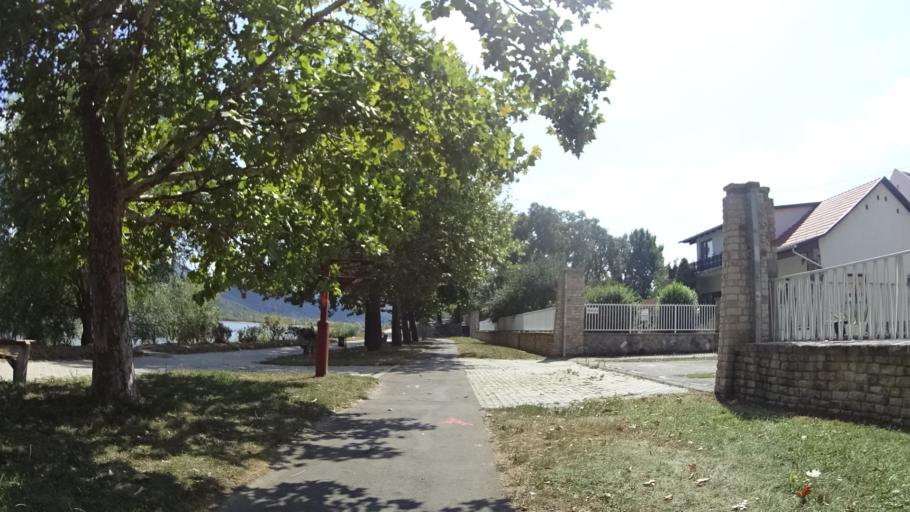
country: HU
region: Pest
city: Nagymaros
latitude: 47.7866
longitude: 18.9598
